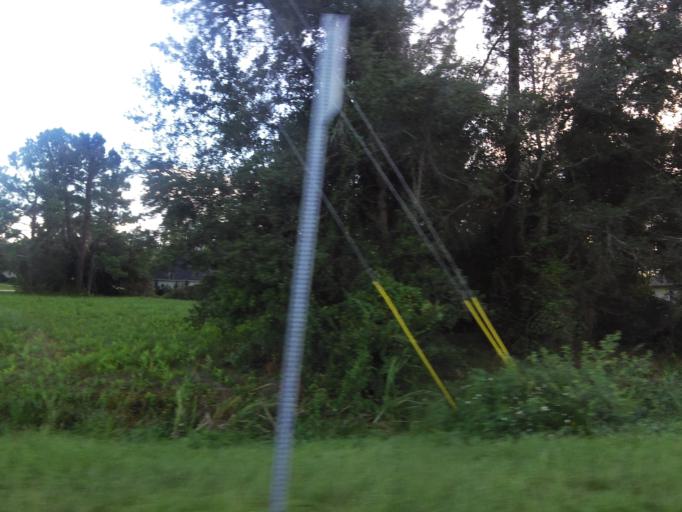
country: US
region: Georgia
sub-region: Camden County
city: St Marys
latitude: 30.7475
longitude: -81.5777
